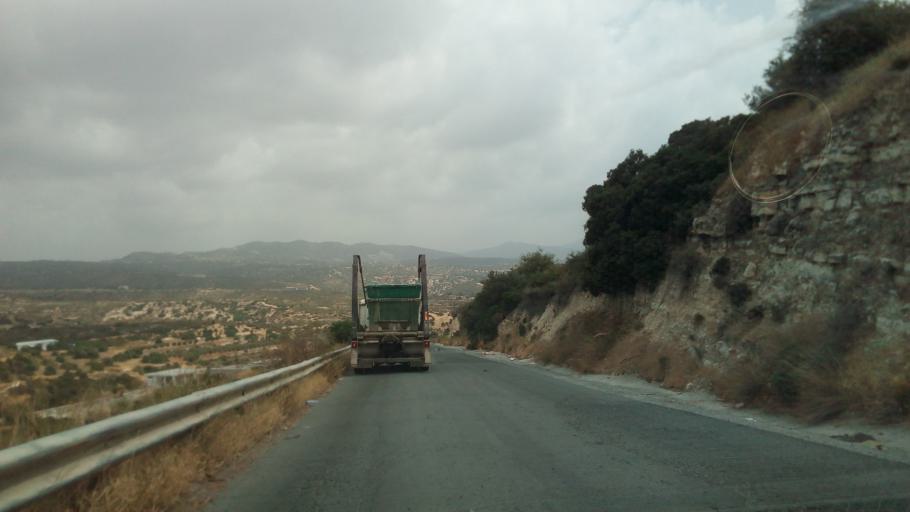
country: CY
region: Limassol
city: Pano Polemidia
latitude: 34.7530
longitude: 32.9540
